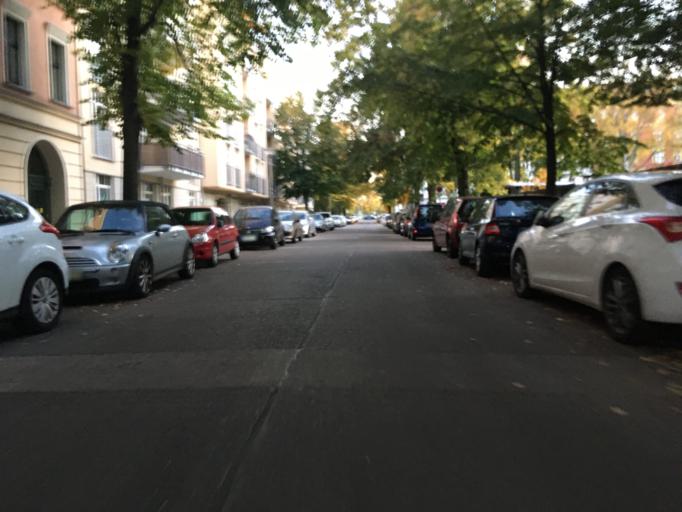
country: DE
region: Berlin
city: Prenzlauer Berg Bezirk
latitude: 52.5549
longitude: 13.4207
